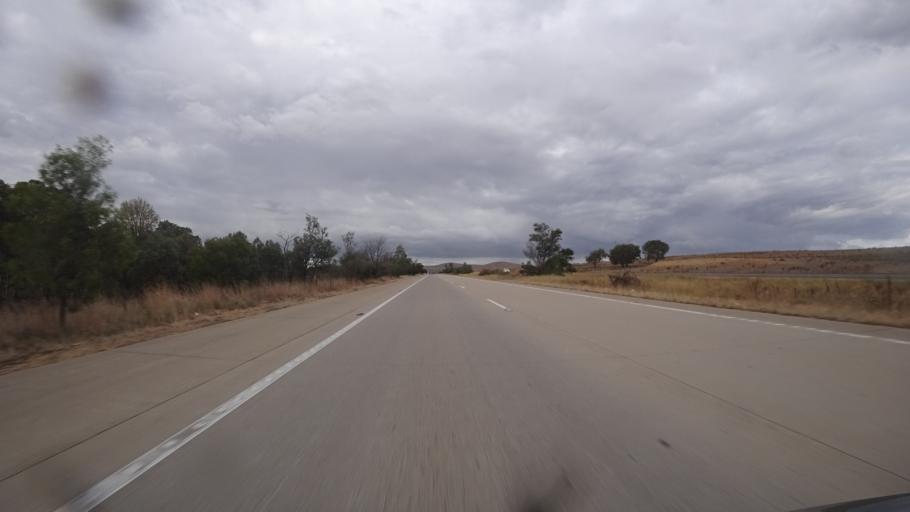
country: AU
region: New South Wales
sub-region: Yass Valley
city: Yass
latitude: -34.8201
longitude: 148.6611
